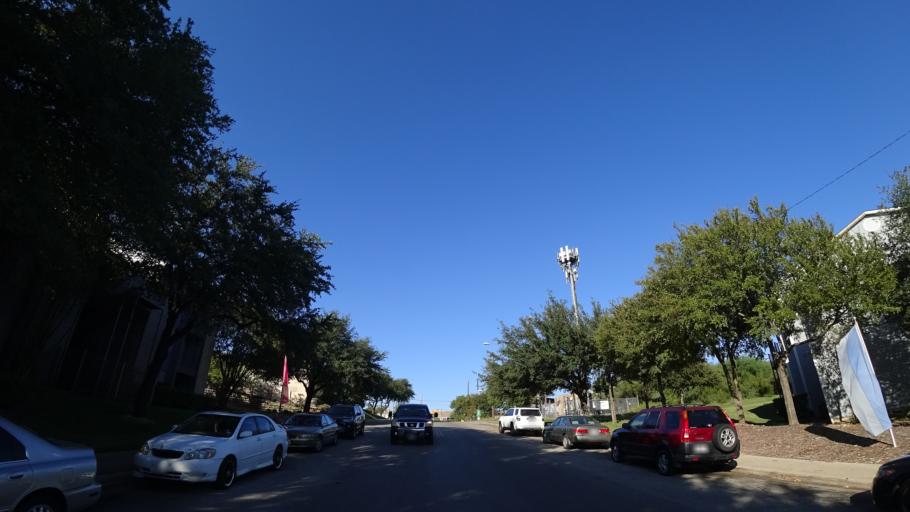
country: US
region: Texas
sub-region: Travis County
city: Austin
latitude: 30.2290
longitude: -97.7322
